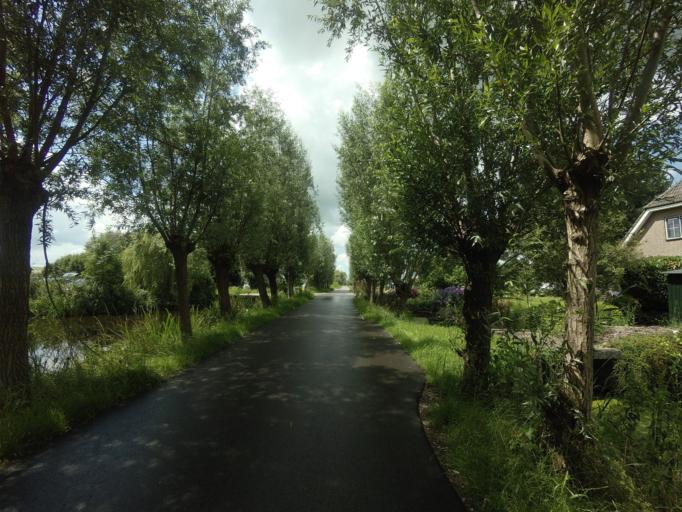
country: NL
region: South Holland
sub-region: Gemeente Vlist
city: Vlist
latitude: 51.9631
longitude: 4.7896
